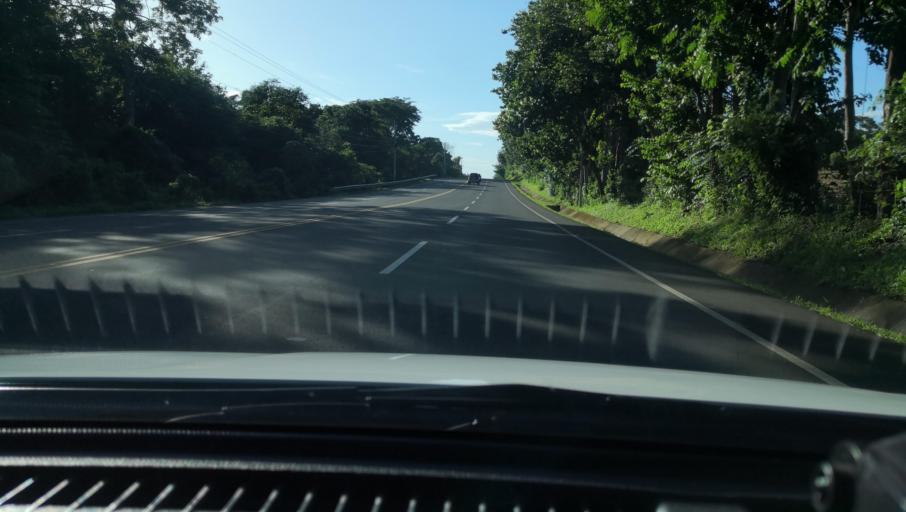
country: NI
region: Carazo
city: La Paz de Oriente
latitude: 11.8242
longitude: -86.1629
